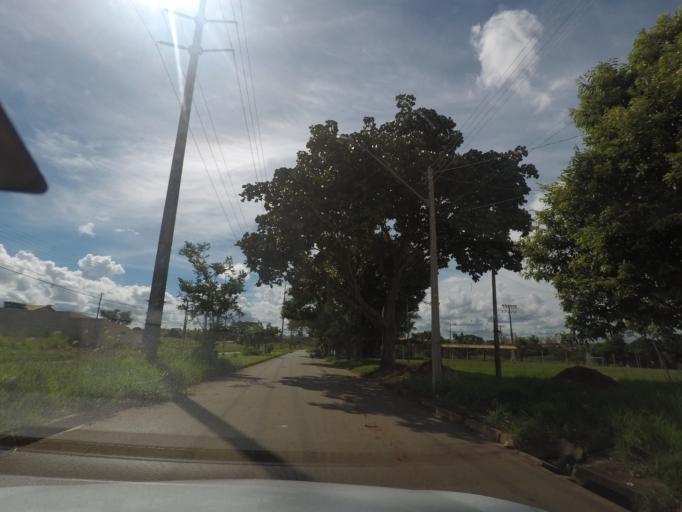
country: BR
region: Goias
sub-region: Goiania
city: Goiania
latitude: -16.7256
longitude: -49.3418
